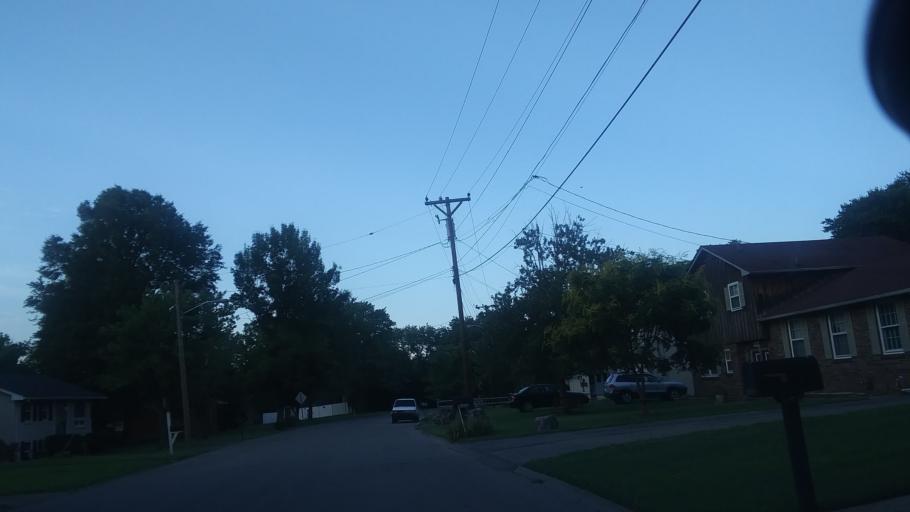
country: US
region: Tennessee
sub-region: Rutherford County
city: La Vergne
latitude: 36.0629
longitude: -86.6669
